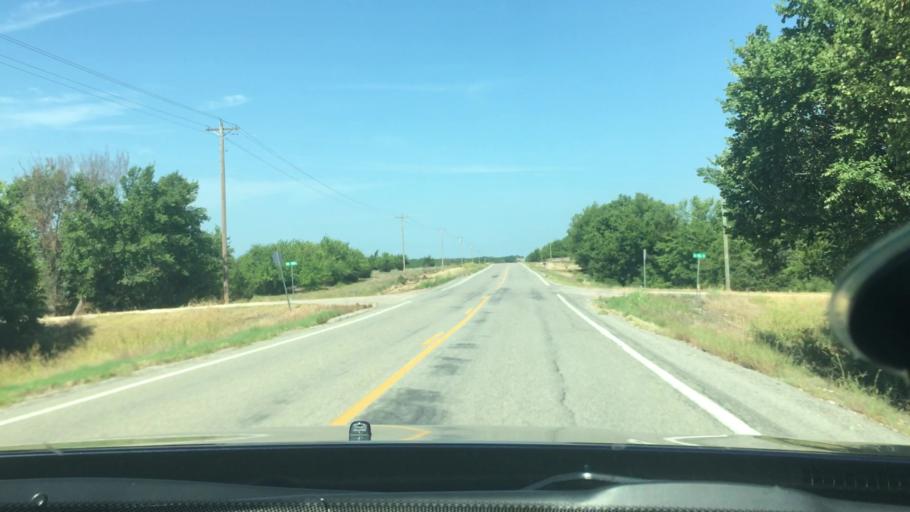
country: US
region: Oklahoma
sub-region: Marshall County
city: Kingston
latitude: 33.9984
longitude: -96.8127
